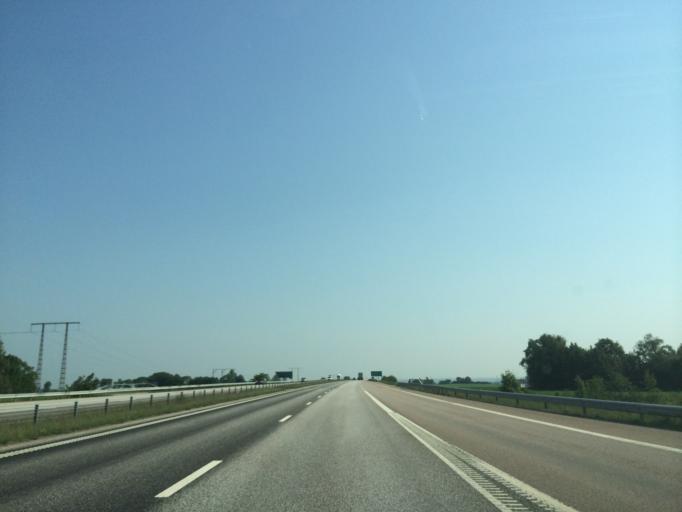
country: SE
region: Skane
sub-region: Astorps Kommun
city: Astorp
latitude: 56.1471
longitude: 12.9380
